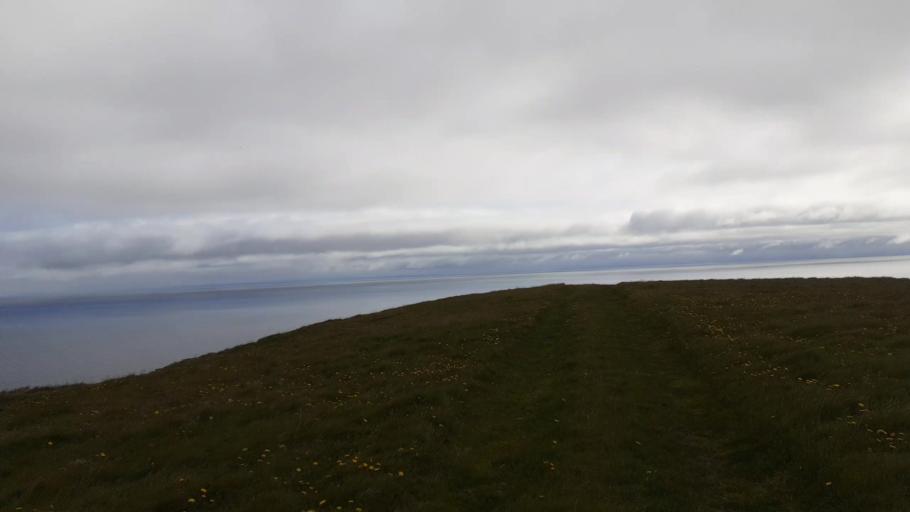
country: IS
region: Northeast
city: Dalvik
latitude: 66.5375
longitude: -17.9816
